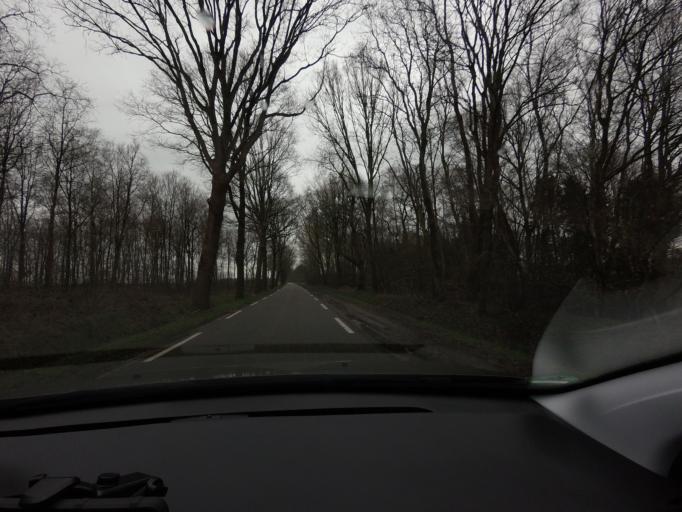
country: NL
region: Drenthe
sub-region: Gemeente Hoogeveen
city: Hoogeveen
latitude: 52.8002
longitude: 6.5174
